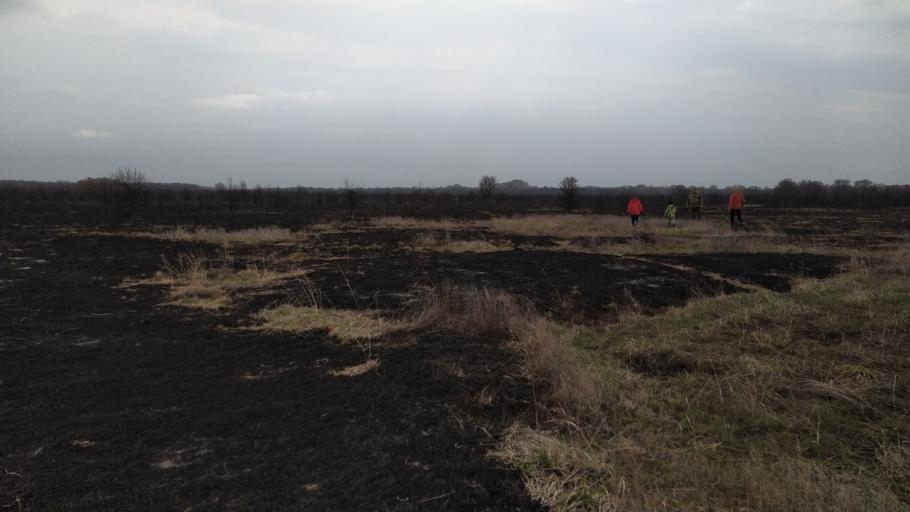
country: RU
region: Rostov
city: Semikarakorsk
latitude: 47.5498
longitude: 40.6782
